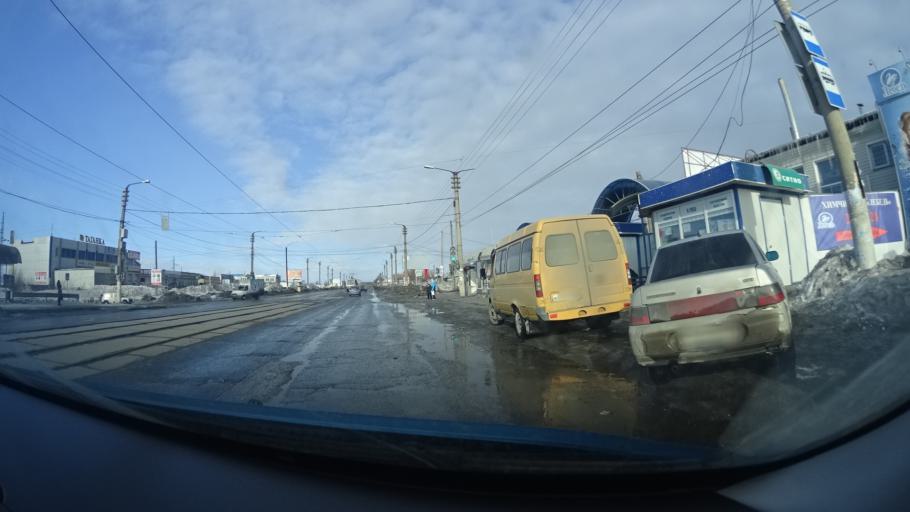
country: RU
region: Chelyabinsk
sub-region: Gorod Magnitogorsk
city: Magnitogorsk
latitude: 53.4384
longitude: 58.9959
